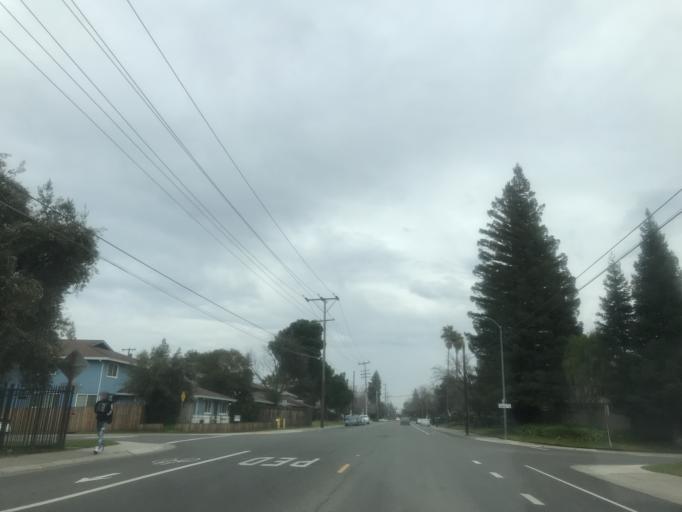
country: US
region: California
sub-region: Sacramento County
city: Arden-Arcade
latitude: 38.5815
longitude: -121.4056
